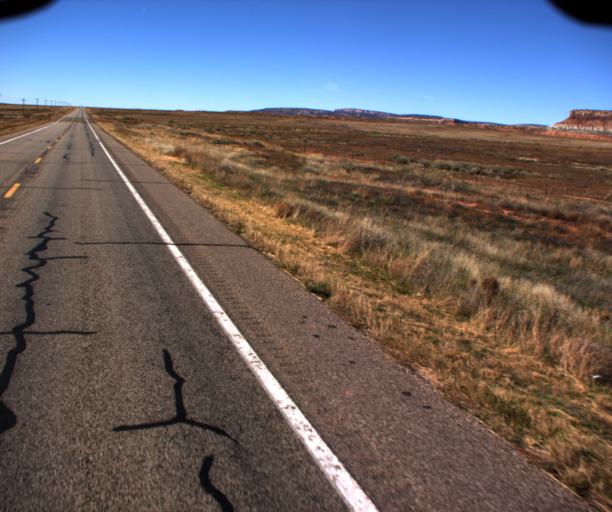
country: US
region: Arizona
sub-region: Coconino County
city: Fredonia
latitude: 36.8955
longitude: -112.6102
